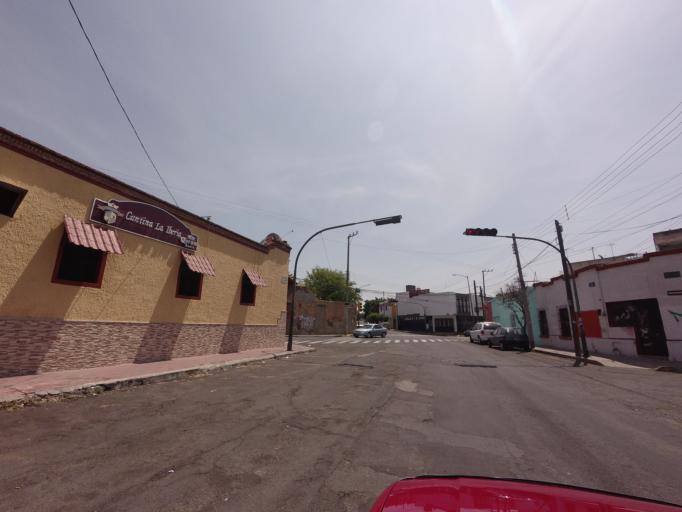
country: MX
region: Jalisco
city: Guadalajara
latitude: 20.6827
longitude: -103.3410
